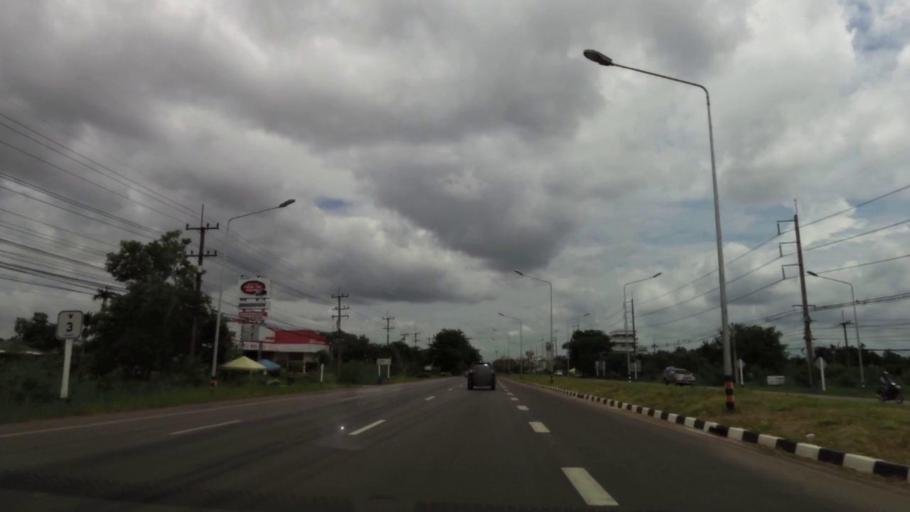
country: TH
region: Rayong
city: Klaeng
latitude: 12.7859
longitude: 101.6759
